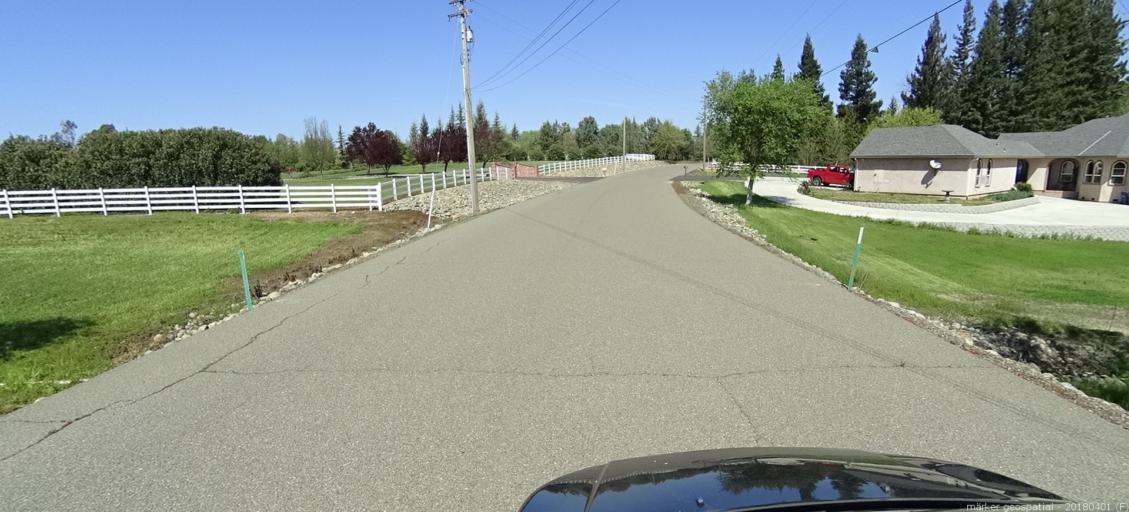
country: US
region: California
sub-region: Sacramento County
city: Wilton
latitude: 38.4145
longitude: -121.2272
